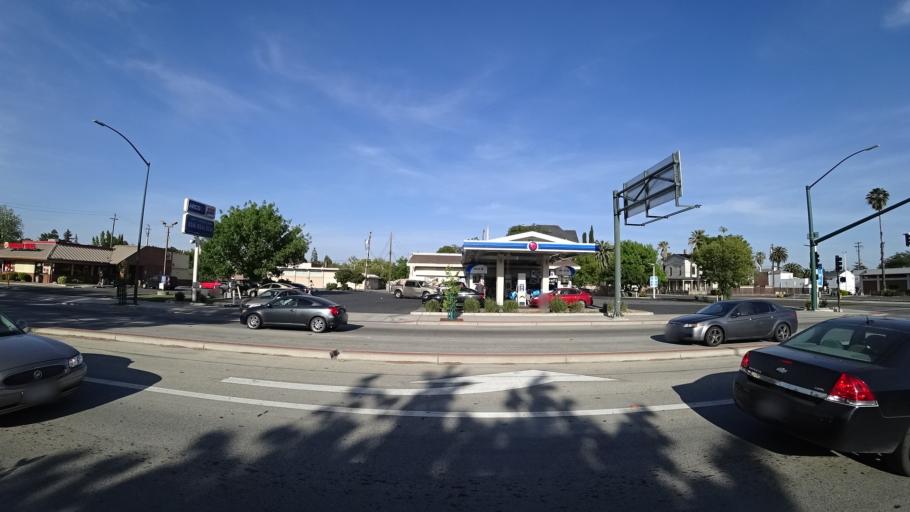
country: US
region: California
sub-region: Yuba County
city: Marysville
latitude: 39.1428
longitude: -121.5910
